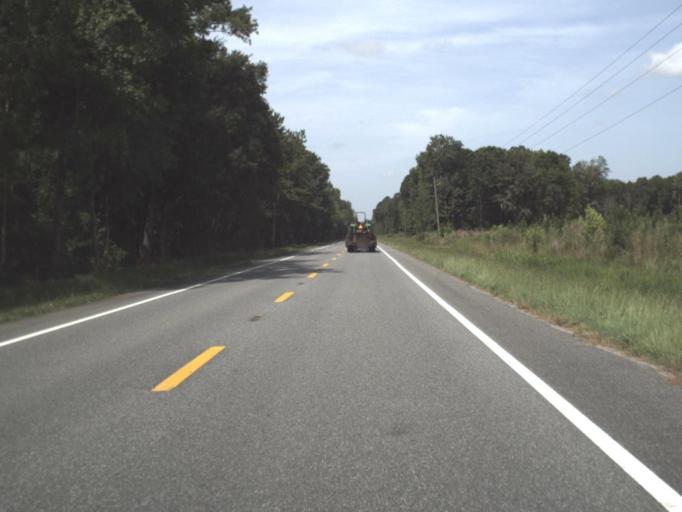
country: US
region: Florida
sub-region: Lafayette County
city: Mayo
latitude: 29.9690
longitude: -83.2178
